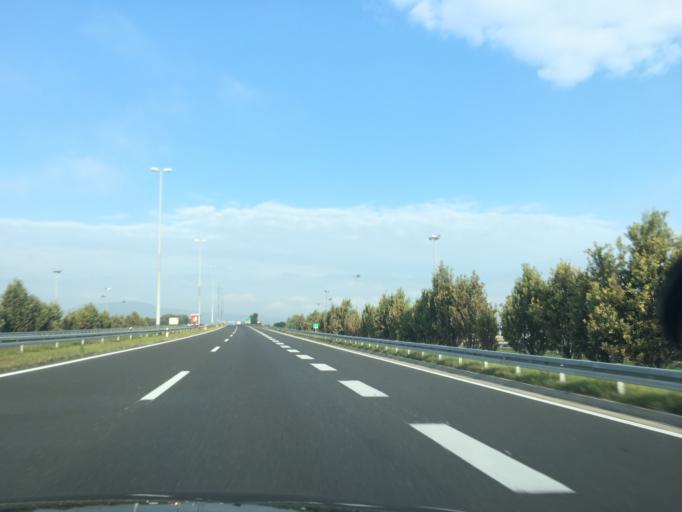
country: HR
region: Zagrebacka
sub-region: Grad Samobor
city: Samobor
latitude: 45.8260
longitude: 15.7392
